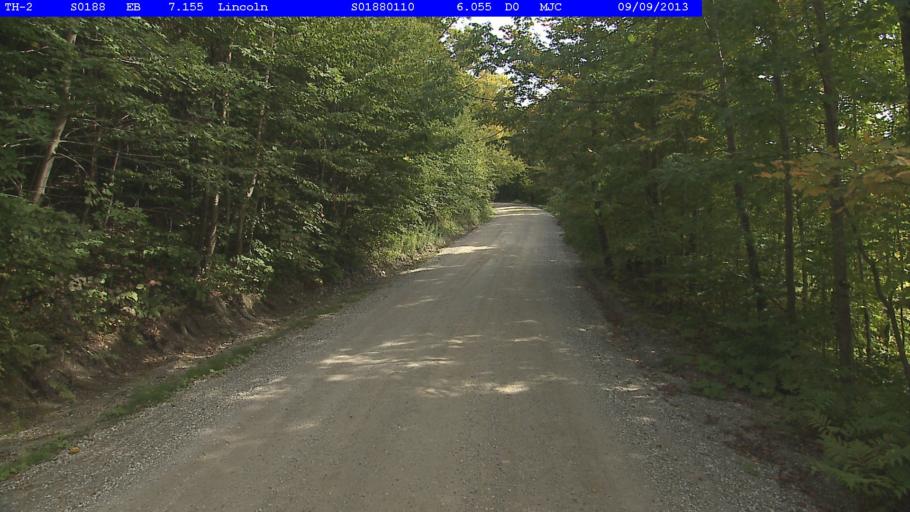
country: US
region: Vermont
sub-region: Addison County
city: Bristol
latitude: 44.0913
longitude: -72.9376
